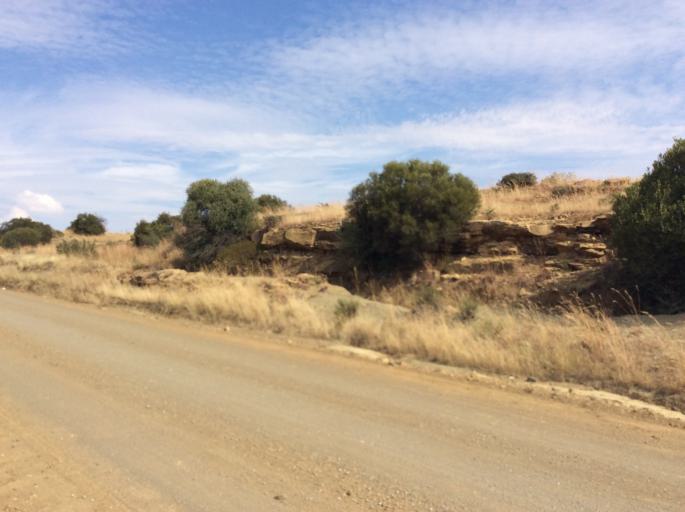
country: ZA
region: Orange Free State
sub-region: Xhariep District Municipality
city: Dewetsdorp
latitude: -29.5847
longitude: 26.6581
